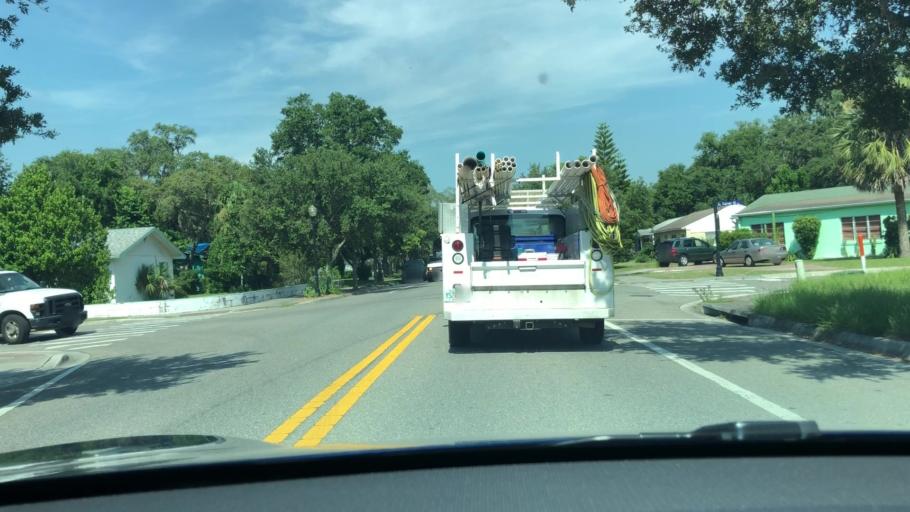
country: US
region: Florida
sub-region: Orange County
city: Winter Park
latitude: 28.6040
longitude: -81.3587
